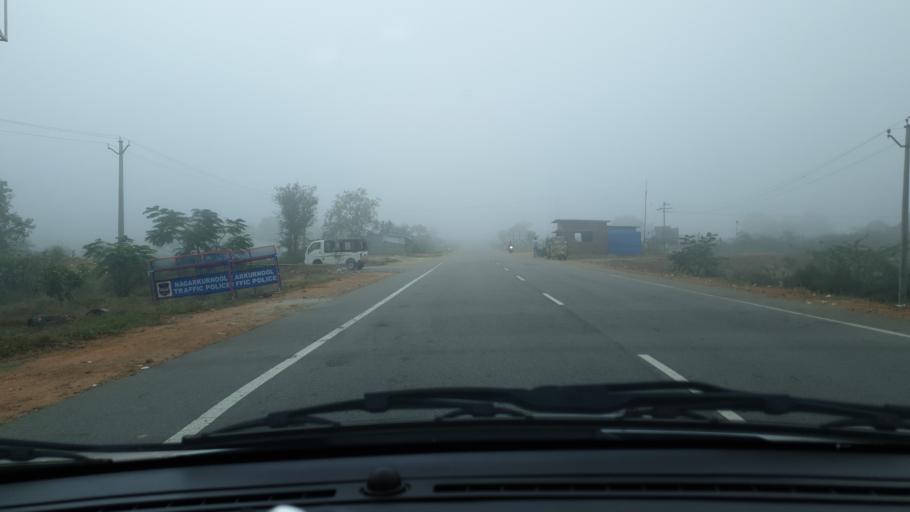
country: IN
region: Telangana
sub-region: Nalgonda
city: Devarkonda
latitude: 16.6207
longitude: 78.6722
